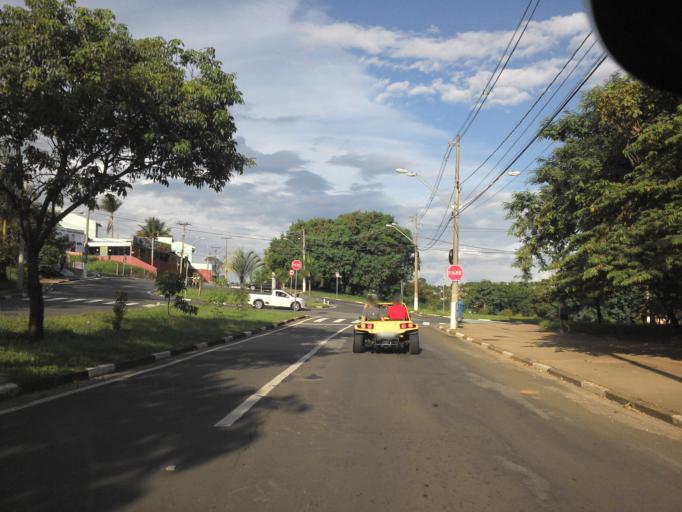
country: BR
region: Sao Paulo
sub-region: Campinas
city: Campinas
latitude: -22.8732
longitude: -47.0414
